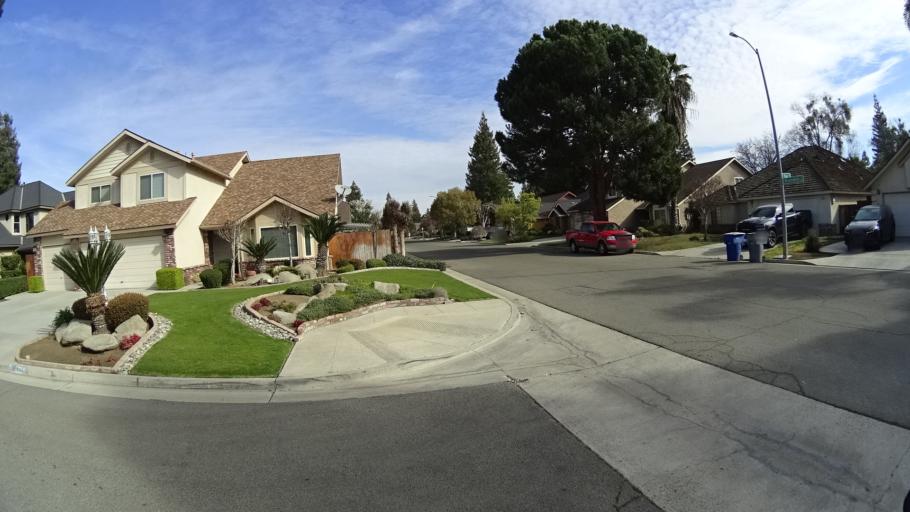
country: US
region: California
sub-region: Fresno County
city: West Park
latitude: 36.8313
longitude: -119.8675
